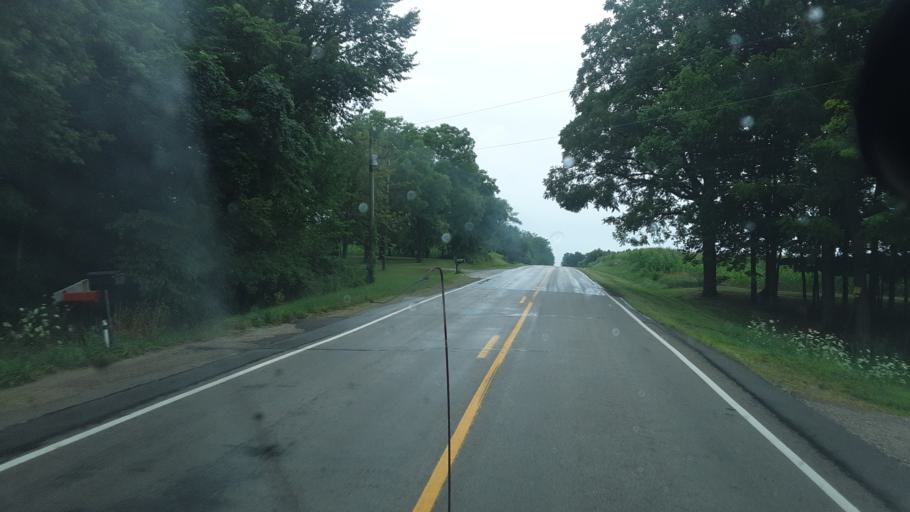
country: US
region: Indiana
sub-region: Steuben County
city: Hamilton
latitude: 41.5588
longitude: -84.8402
